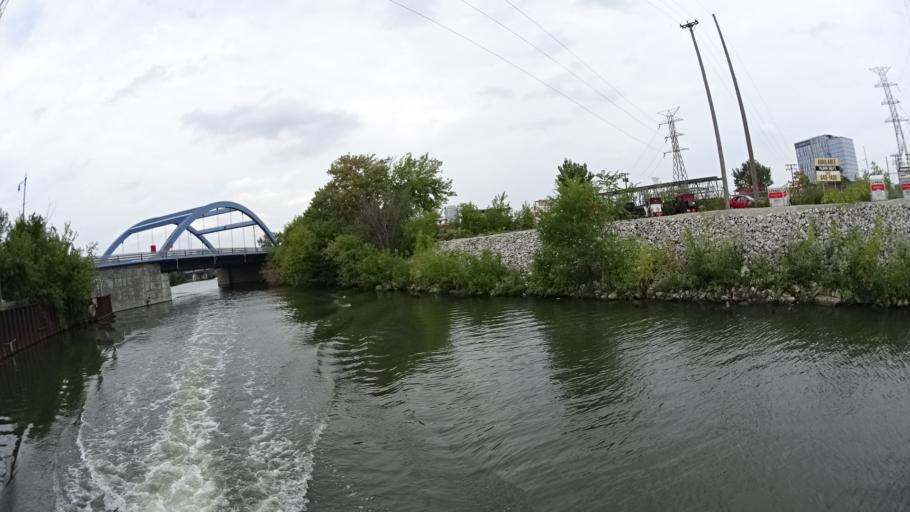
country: US
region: Illinois
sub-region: Cook County
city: Chicago
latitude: 41.9014
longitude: -87.6474
